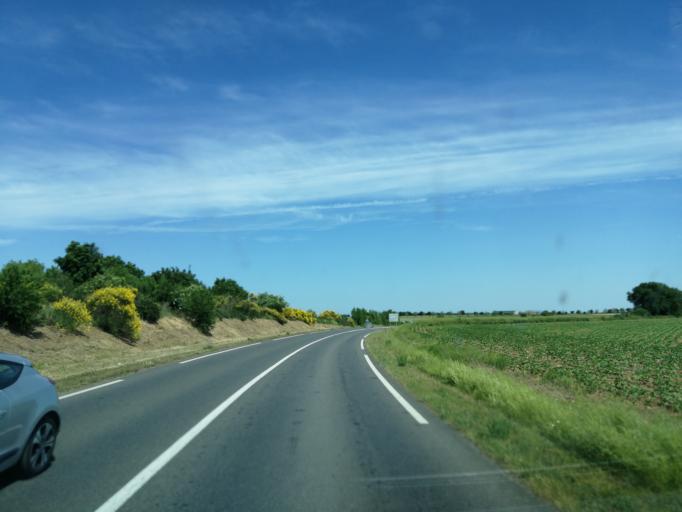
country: FR
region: Poitou-Charentes
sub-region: Departement des Deux-Sevres
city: Saint-Jean-de-Thouars
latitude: 46.9540
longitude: -0.2193
